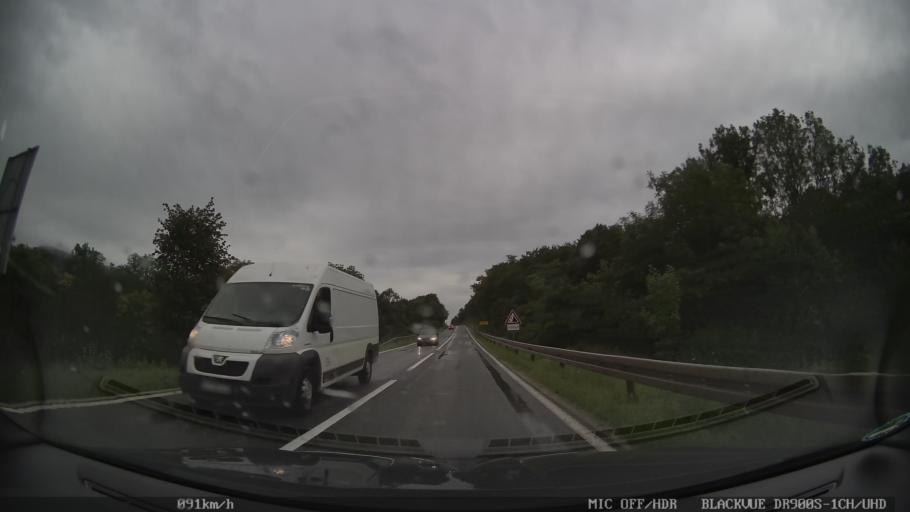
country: HR
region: Licko-Senjska
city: Brinje
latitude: 44.9635
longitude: 15.0803
